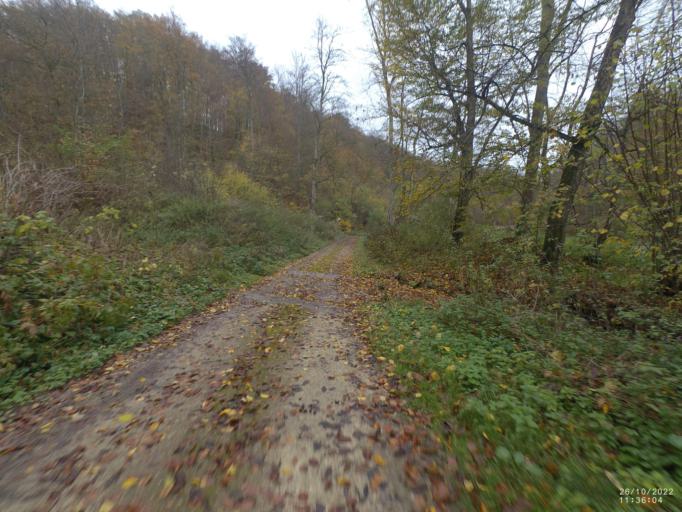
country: DE
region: Baden-Wuerttemberg
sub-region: Regierungsbezirk Stuttgart
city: Bohmenkirch
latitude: 48.6775
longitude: 9.8908
